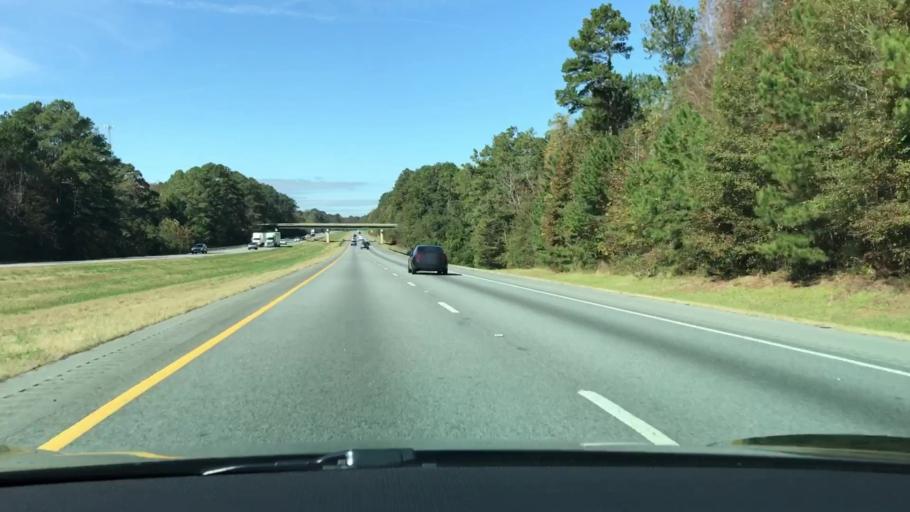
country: US
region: Georgia
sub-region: Morgan County
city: Madison
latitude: 33.5717
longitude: -83.5216
